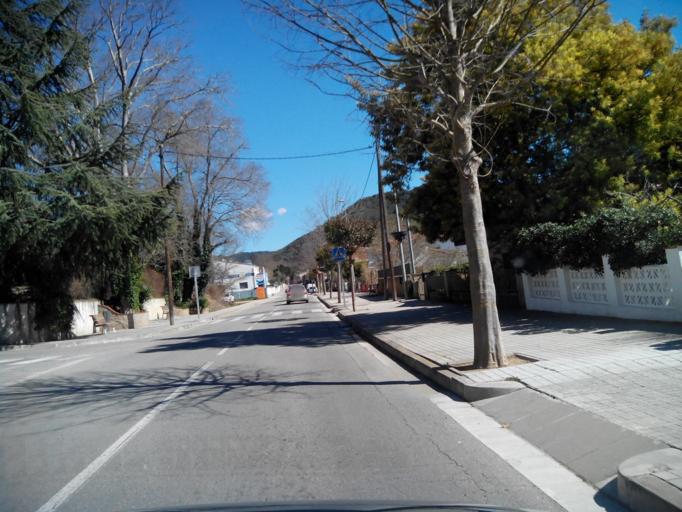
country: ES
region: Catalonia
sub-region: Provincia de Barcelona
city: Dosrius
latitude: 41.5984
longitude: 2.4420
